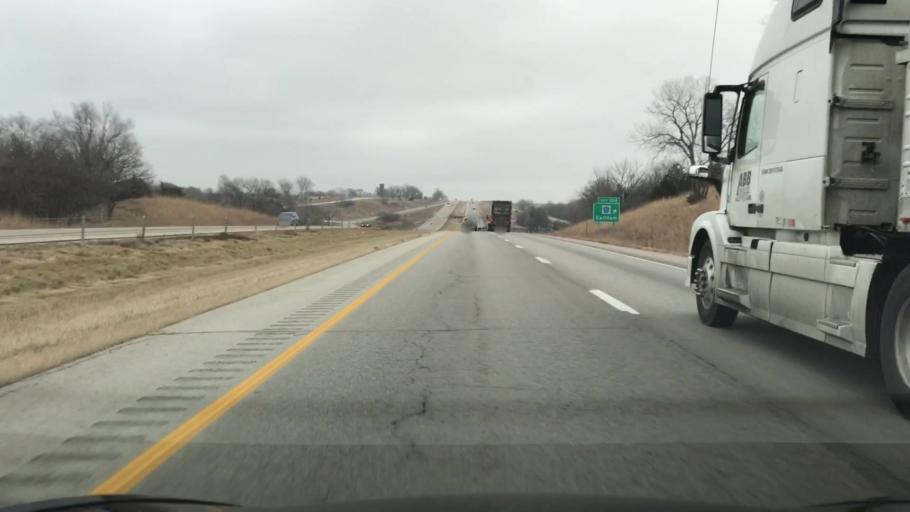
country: US
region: Iowa
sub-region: Madison County
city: Earlham
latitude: 41.5176
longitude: -94.1308
